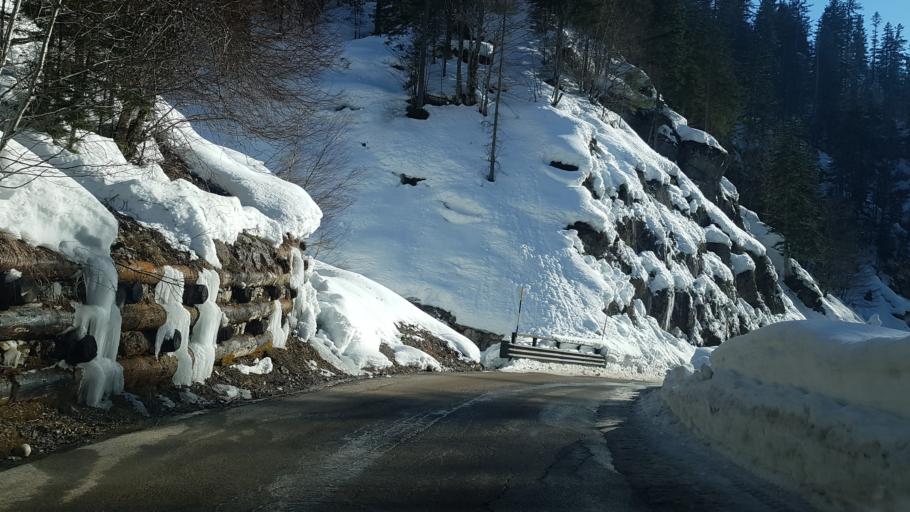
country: IT
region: Friuli Venezia Giulia
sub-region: Provincia di Udine
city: Malborghetto
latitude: 46.5273
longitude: 13.4753
